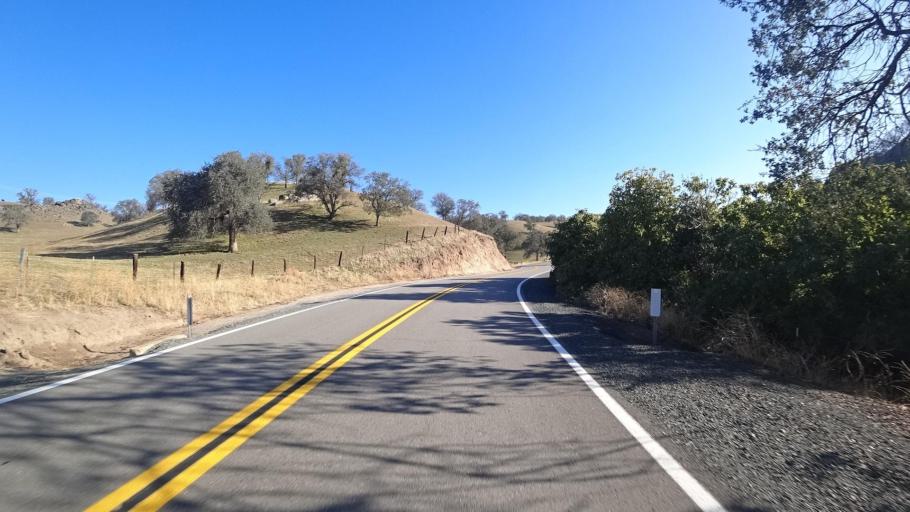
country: US
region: California
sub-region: Kern County
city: Alta Sierra
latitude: 35.7140
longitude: -118.8203
